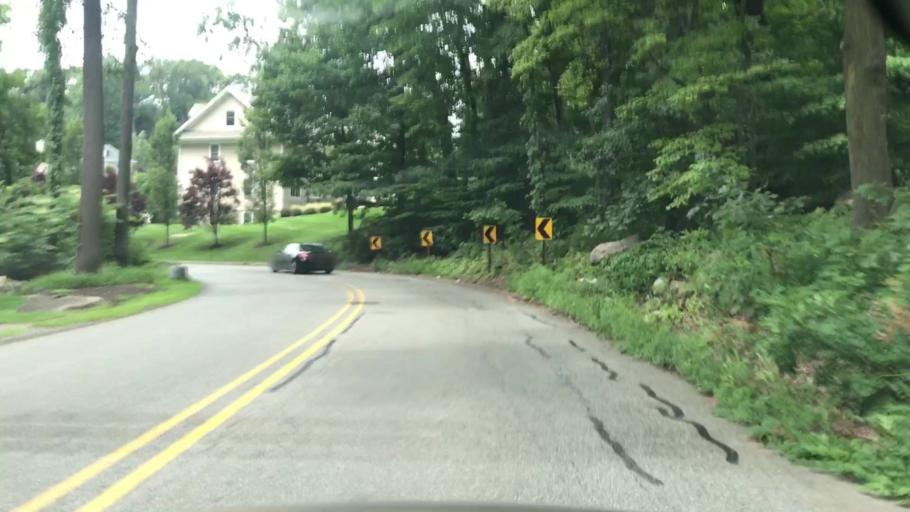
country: US
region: New Jersey
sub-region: Morris County
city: Mountain Lakes
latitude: 40.9013
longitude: -74.4217
